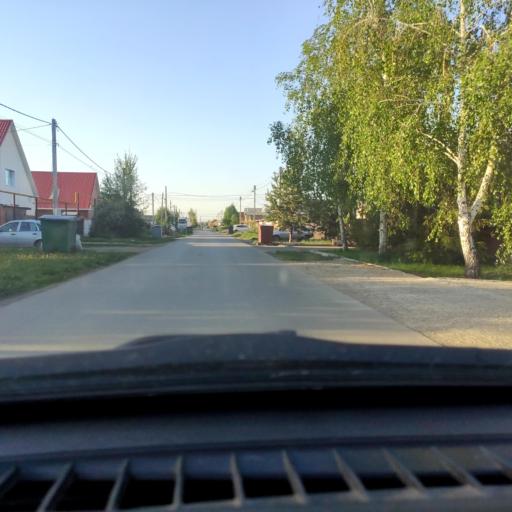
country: RU
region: Samara
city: Tol'yatti
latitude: 53.5617
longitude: 49.4026
